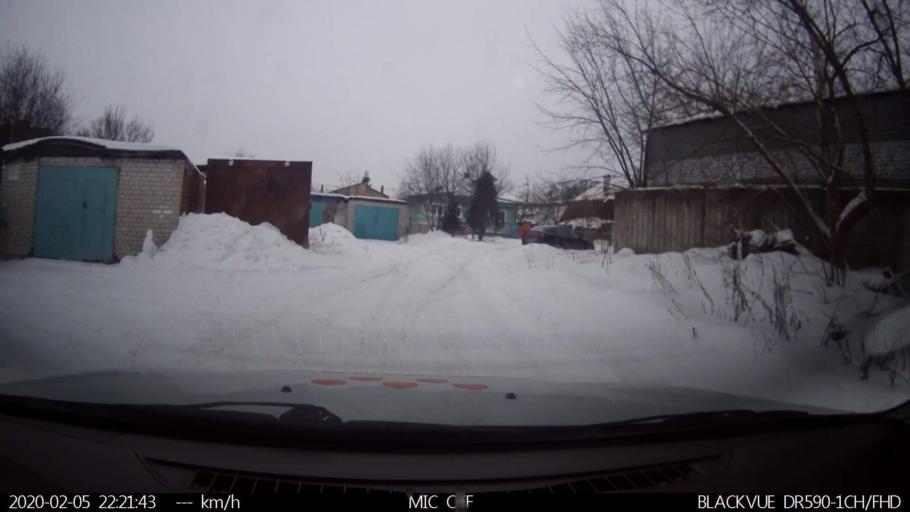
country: RU
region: Nizjnij Novgorod
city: Pervomaysk
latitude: 54.7605
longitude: 44.0007
